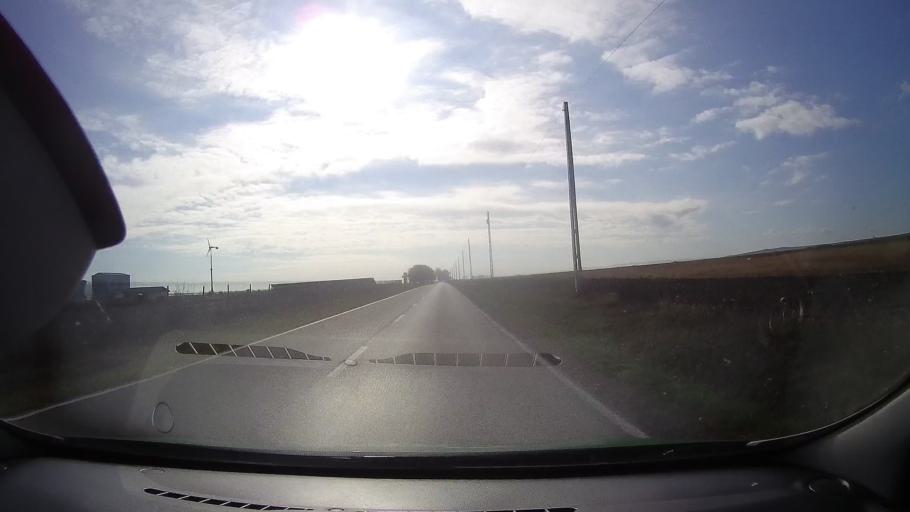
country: RO
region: Tulcea
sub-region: Comuna Valea Nucarilor
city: Agighiol
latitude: 45.0201
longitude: 28.8828
